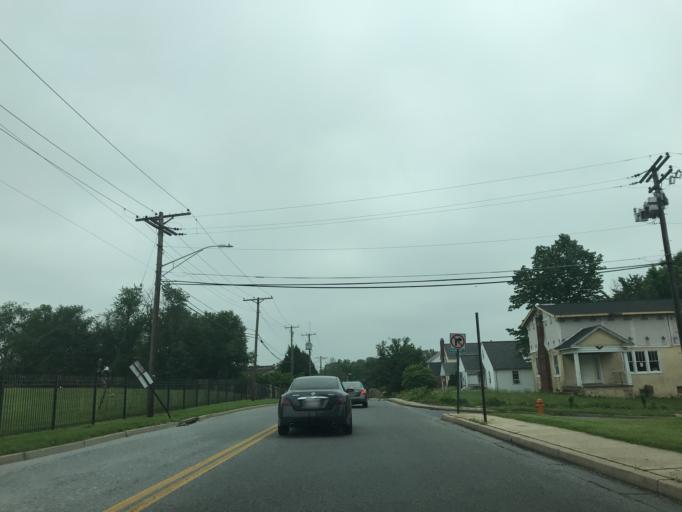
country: US
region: Maryland
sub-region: Baltimore County
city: Charlestown
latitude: 39.2693
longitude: -76.6918
